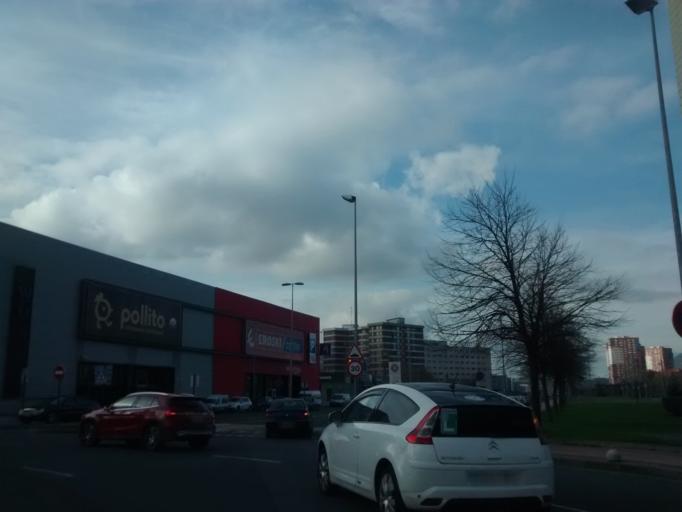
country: ES
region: Basque Country
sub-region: Bizkaia
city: Barakaldo
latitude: 43.2856
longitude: -2.9942
